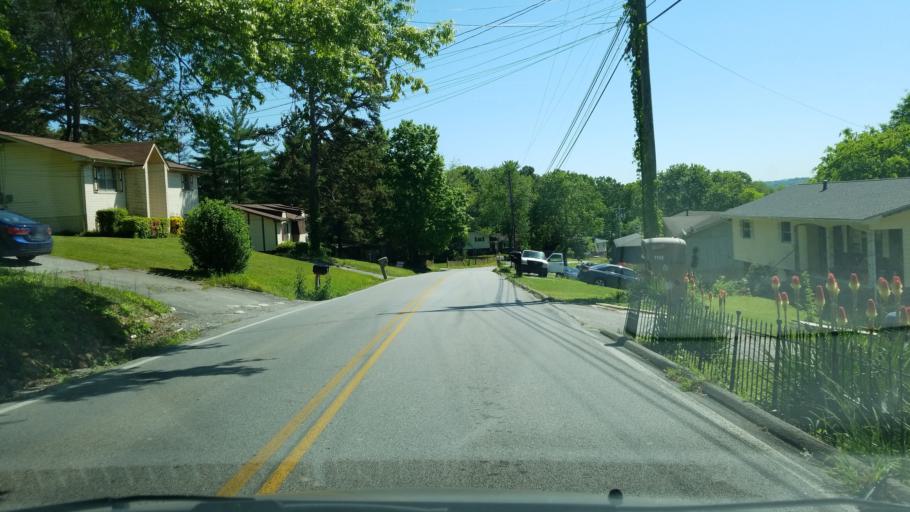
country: US
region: Tennessee
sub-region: Hamilton County
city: Middle Valley
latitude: 35.1762
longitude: -85.2191
